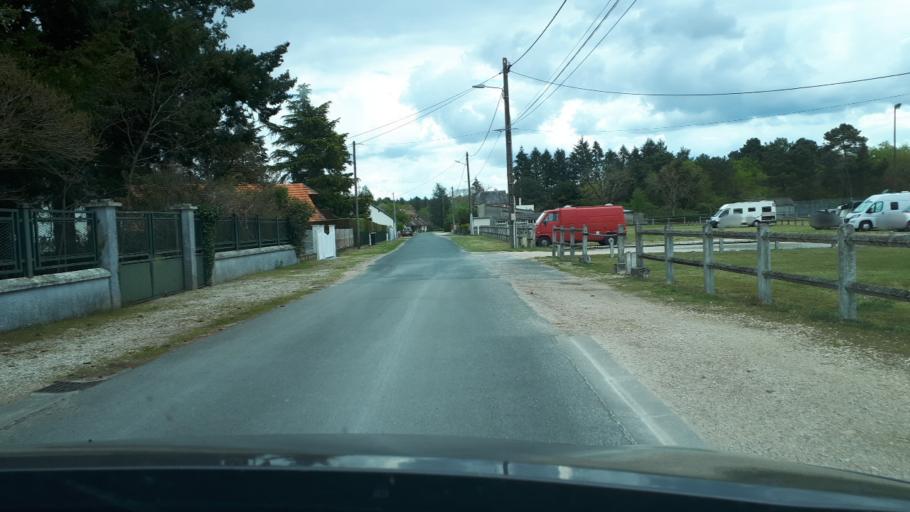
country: FR
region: Centre
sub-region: Departement du Loir-et-Cher
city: Souesmes
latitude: 47.5094
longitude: 2.1545
